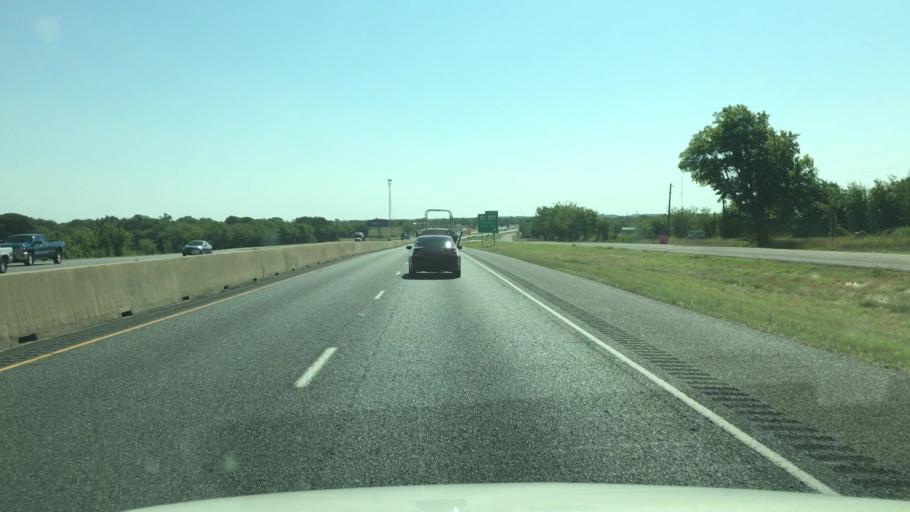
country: US
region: Texas
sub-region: Hunt County
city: Commerce
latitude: 33.1310
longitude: -95.9573
